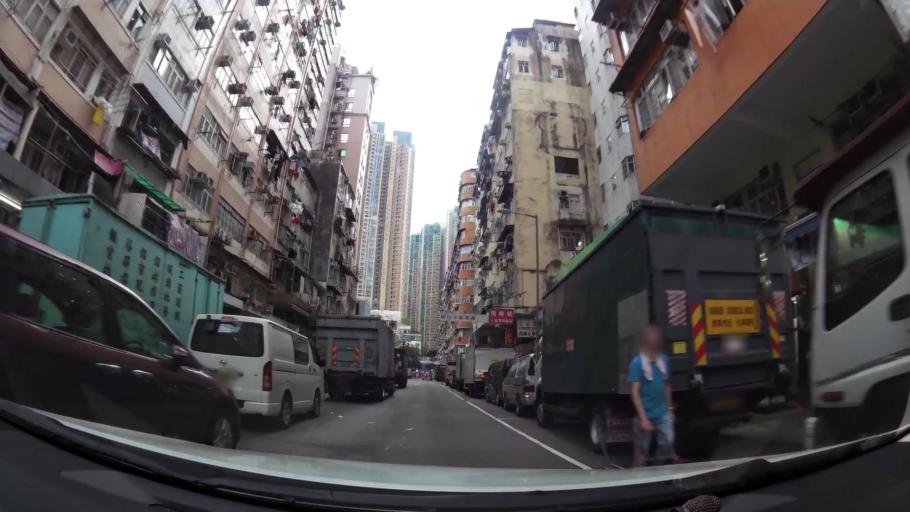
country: HK
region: Sham Shui Po
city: Sham Shui Po
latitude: 22.3208
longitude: 114.1642
